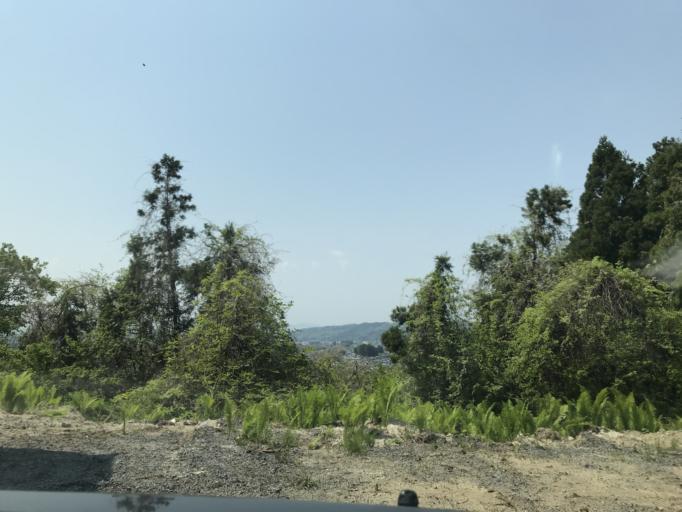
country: JP
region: Iwate
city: Ichinoseki
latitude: 38.9224
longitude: 141.1257
